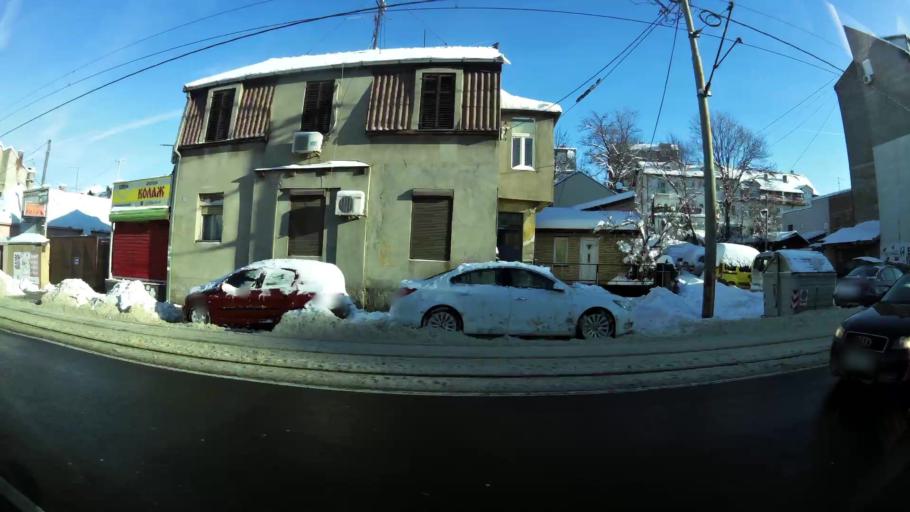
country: RS
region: Central Serbia
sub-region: Belgrade
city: Palilula
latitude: 44.7914
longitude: 20.5121
